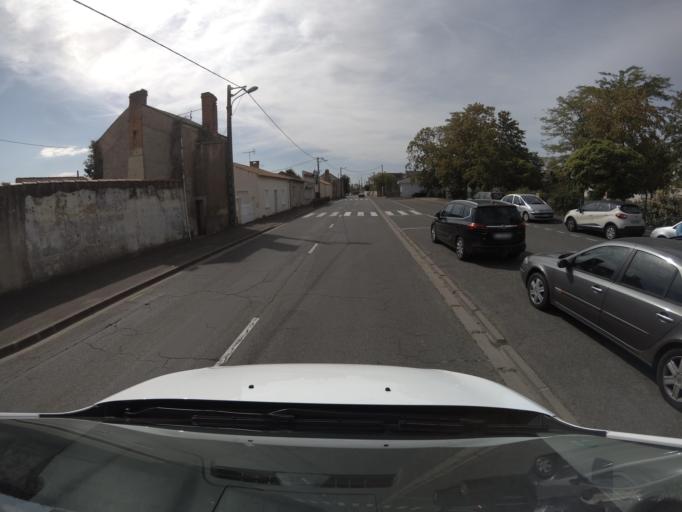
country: FR
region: Poitou-Charentes
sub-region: Departement des Deux-Sevres
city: Thouars
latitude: 46.9764
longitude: -0.2016
